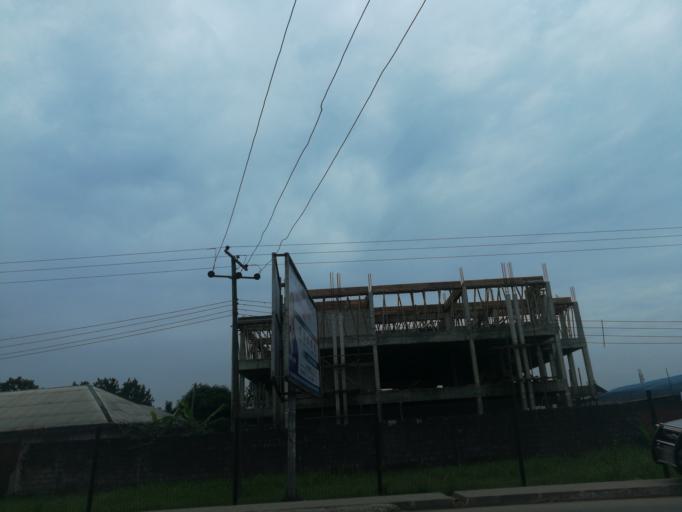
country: NG
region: Rivers
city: Port Harcourt
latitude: 4.8424
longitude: 6.9840
